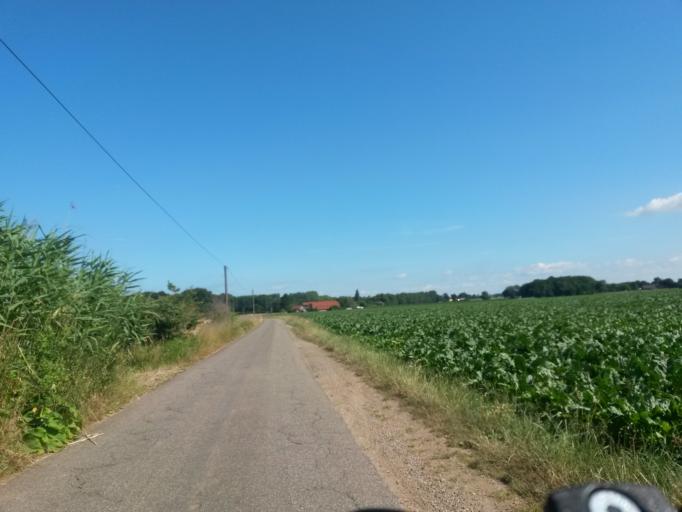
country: DE
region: North Rhine-Westphalia
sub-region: Regierungsbezirk Dusseldorf
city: Wachtendonk
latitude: 51.3834
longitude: 6.3556
